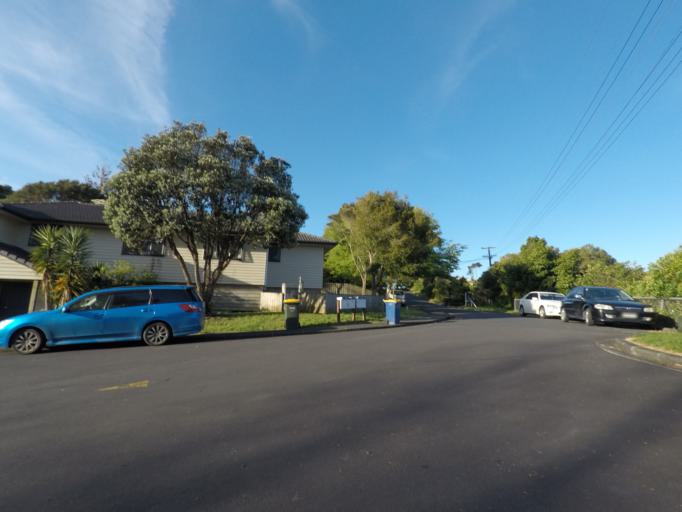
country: NZ
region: Auckland
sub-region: Auckland
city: Rosebank
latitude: -36.8431
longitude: 174.6380
